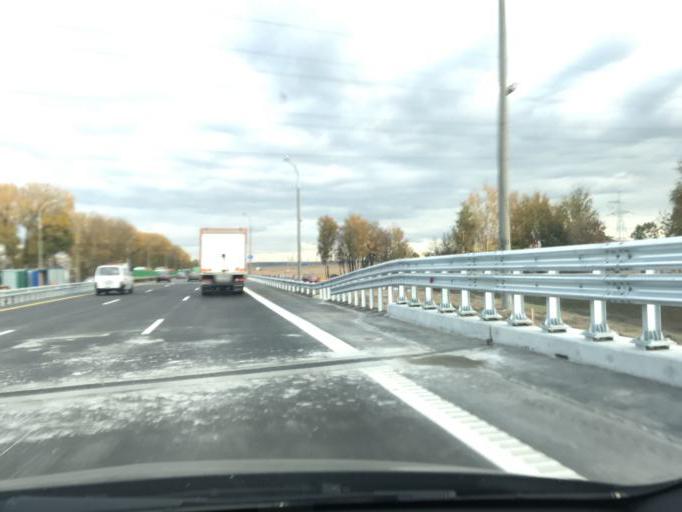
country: BY
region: Minsk
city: Syenitsa
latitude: 53.8330
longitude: 27.5752
